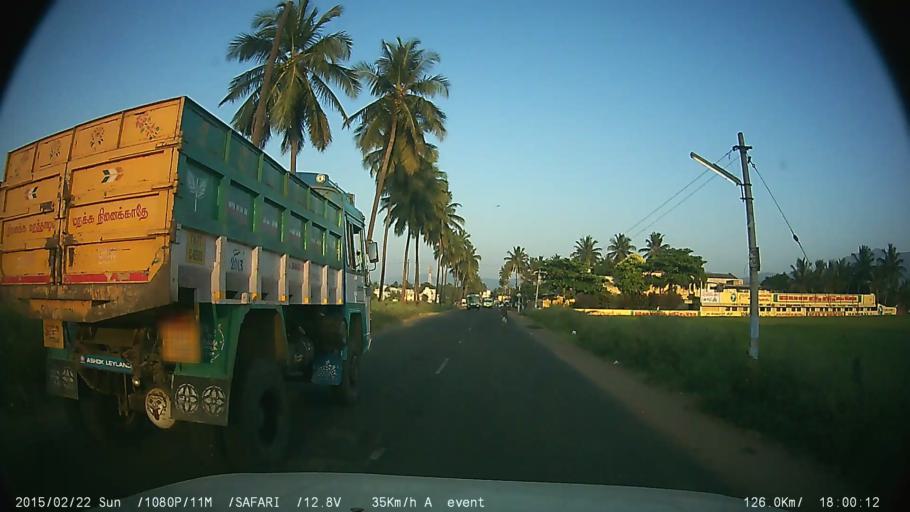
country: IN
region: Tamil Nadu
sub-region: Theni
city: Uttamapalaiyam
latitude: 9.8034
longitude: 77.3295
